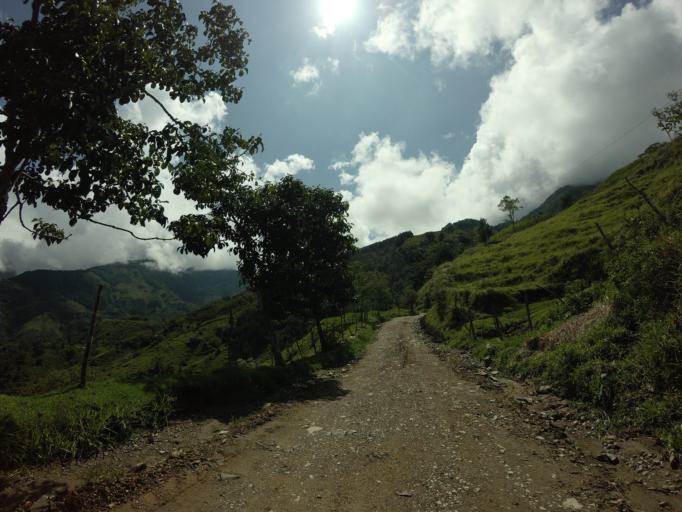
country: CO
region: Caldas
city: Pensilvania
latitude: 5.4709
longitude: -75.1850
